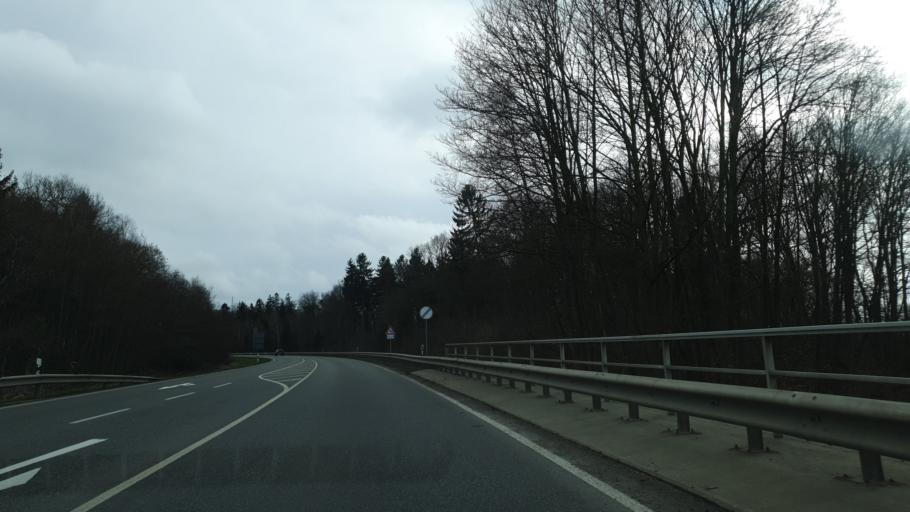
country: DE
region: Rheinland-Pfalz
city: Emmelshausen
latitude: 50.1661
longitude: 7.5680
